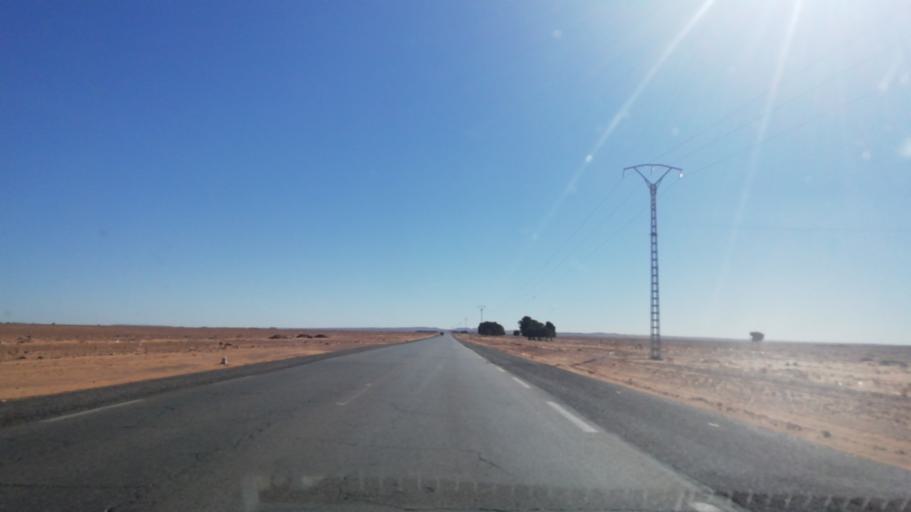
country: DZ
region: Saida
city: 'Ain el Hadjar
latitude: 34.0102
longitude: 0.1183
